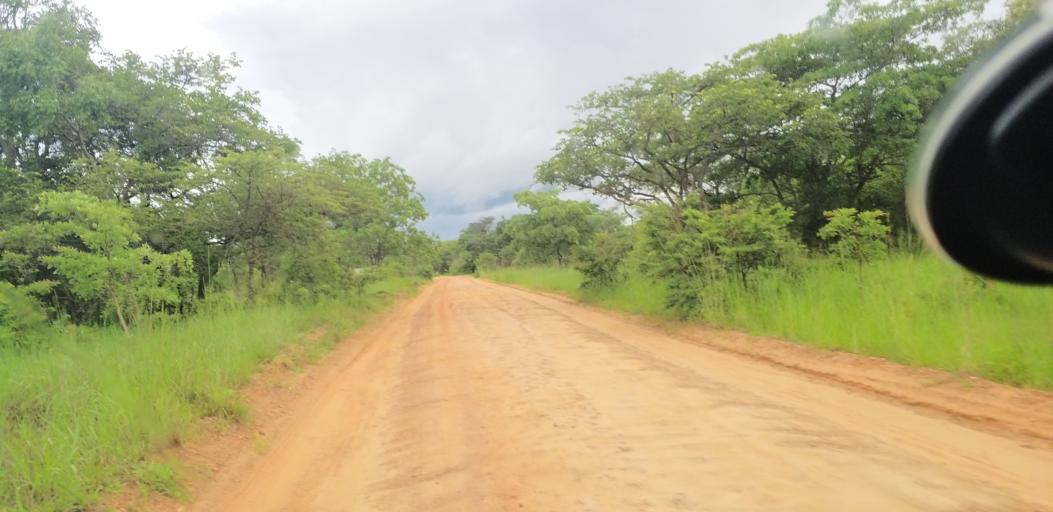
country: ZM
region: Lusaka
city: Chongwe
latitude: -15.1580
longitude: 28.4965
